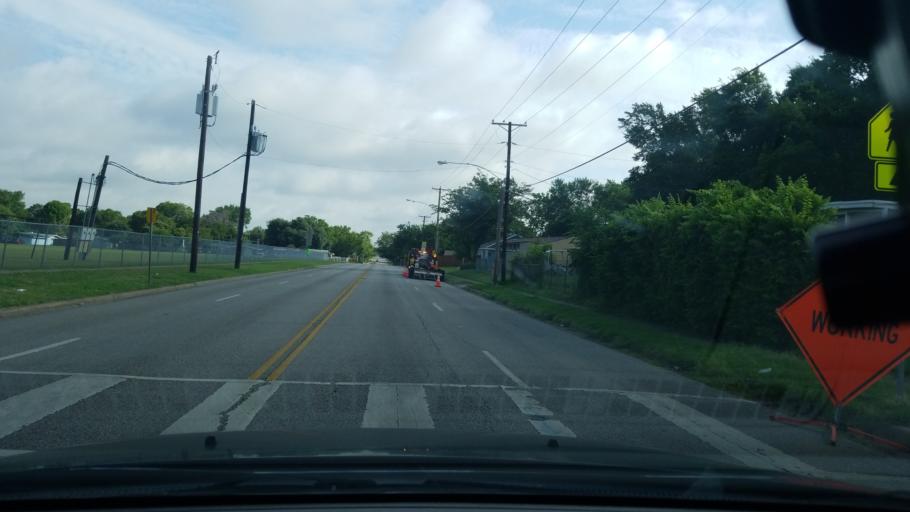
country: US
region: Texas
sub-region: Dallas County
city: Mesquite
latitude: 32.8251
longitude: -96.6681
